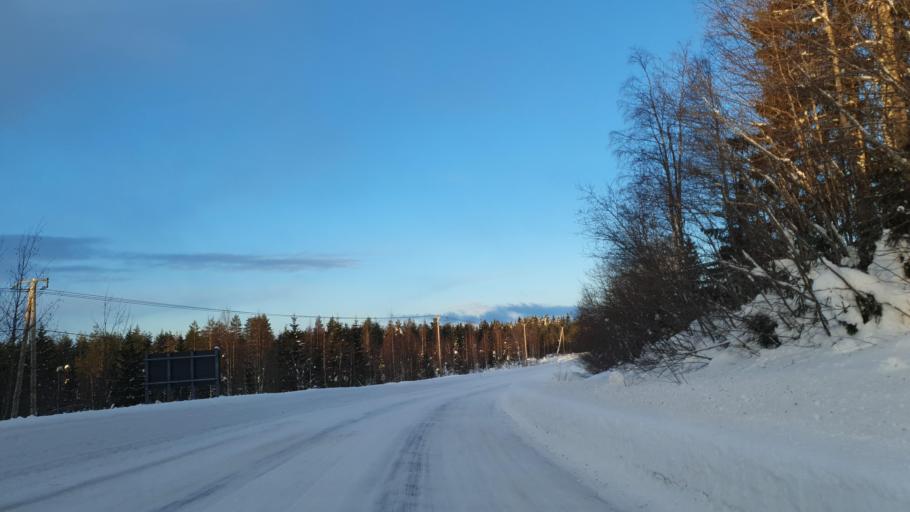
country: FI
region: Kainuu
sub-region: Kajaani
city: Ristijaervi
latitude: 64.3381
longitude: 28.0859
